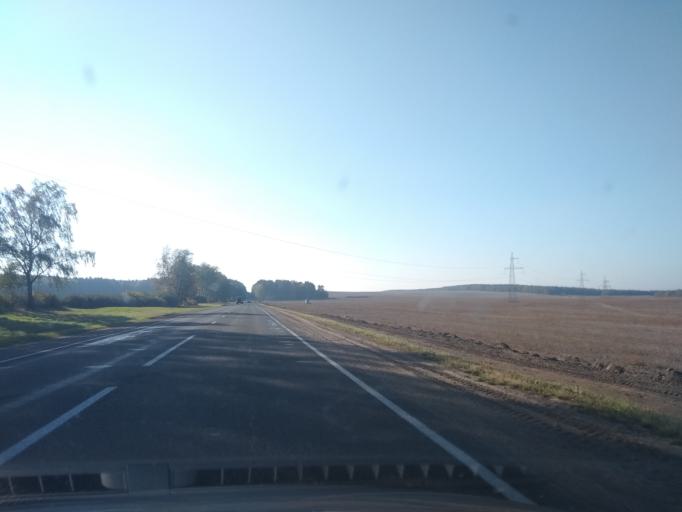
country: BY
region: Grodnenskaya
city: Vawkavysk
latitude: 53.1501
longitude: 24.5530
